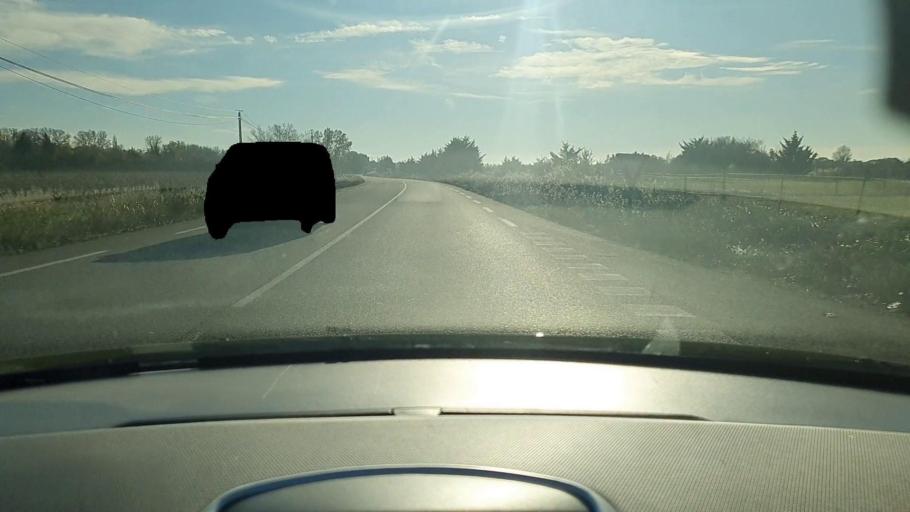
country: FR
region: Languedoc-Roussillon
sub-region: Departement du Gard
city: Beaucaire
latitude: 43.7766
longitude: 4.6215
